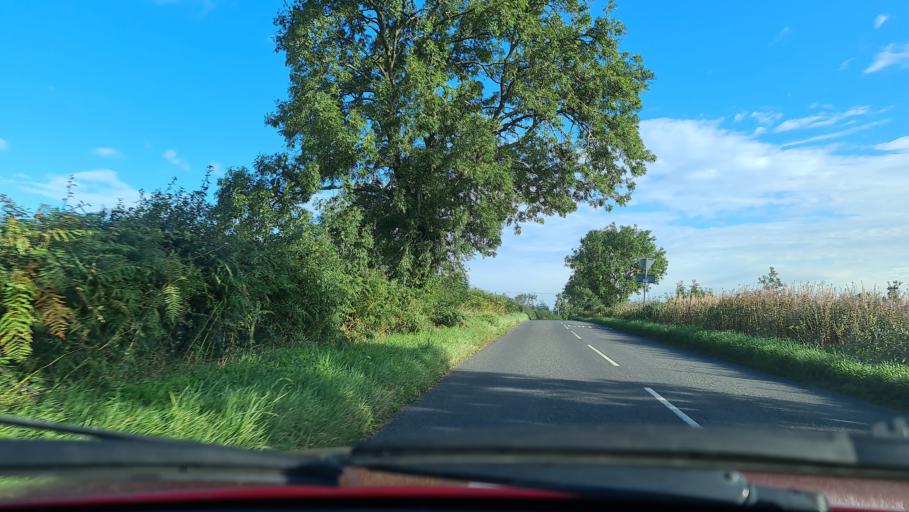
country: GB
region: England
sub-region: Buckinghamshire
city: Stokenchurch
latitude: 51.6856
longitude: -0.8673
